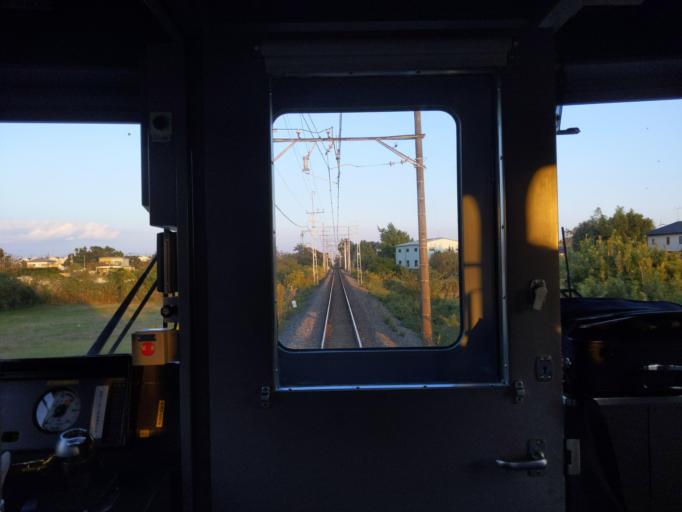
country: JP
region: Saitama
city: Kasukabe
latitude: 35.9800
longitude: 139.7939
